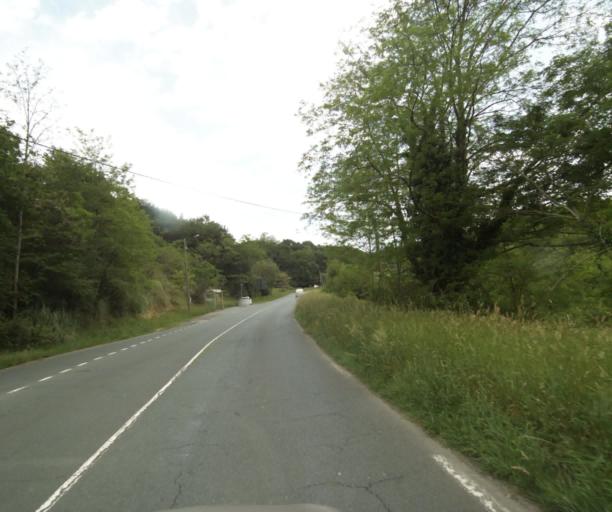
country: FR
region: Aquitaine
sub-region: Departement des Pyrenees-Atlantiques
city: Mouguerre
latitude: 43.4638
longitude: -1.4219
